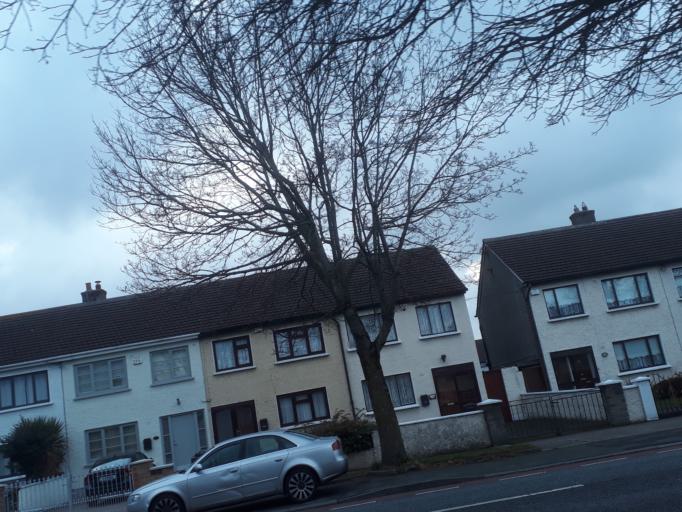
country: IE
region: Leinster
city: Crumlin
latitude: 53.3127
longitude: -6.3281
